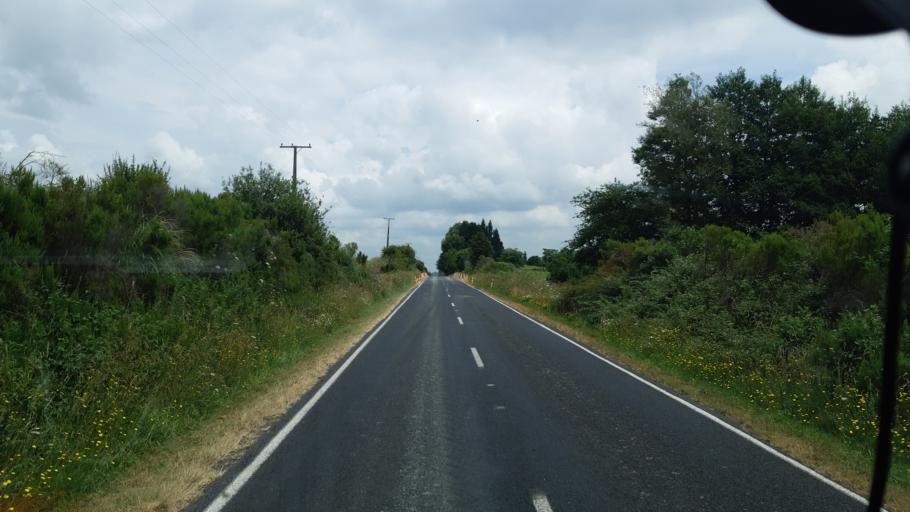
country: NZ
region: Waikato
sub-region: Waipa District
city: Cambridge
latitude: -38.1048
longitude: 175.4754
